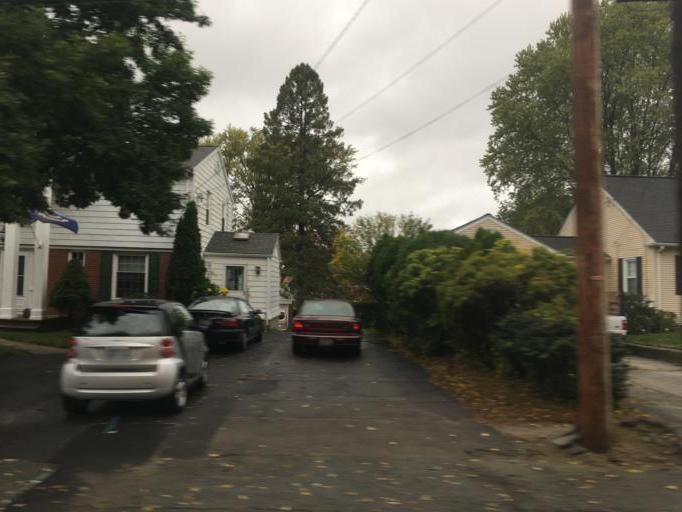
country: US
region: Rhode Island
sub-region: Kent County
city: West Warwick
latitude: 41.7005
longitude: -71.5163
